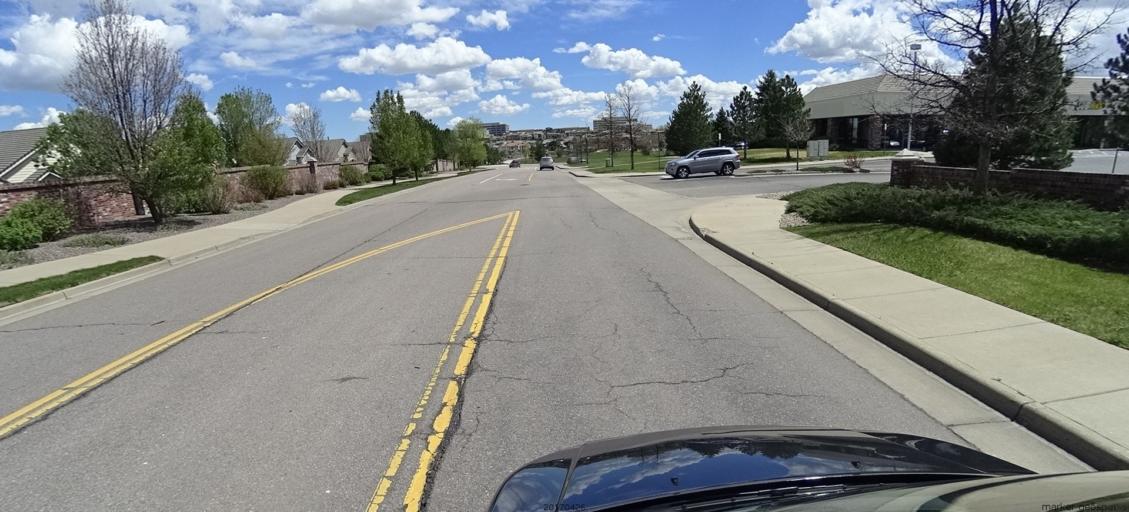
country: US
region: Colorado
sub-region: Adams County
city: Lone Tree
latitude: 39.5390
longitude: -104.8844
